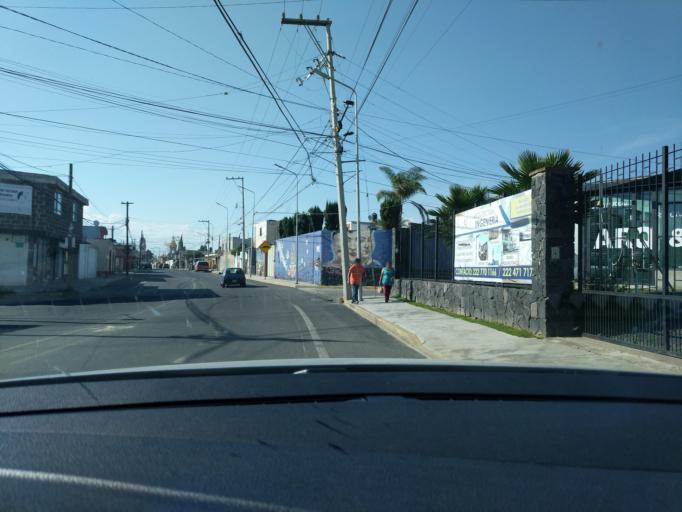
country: MX
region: Puebla
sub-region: San Gregorio Atzompa
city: Chipilo de Francisco Javier Mina
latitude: 19.0277
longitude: -98.3161
